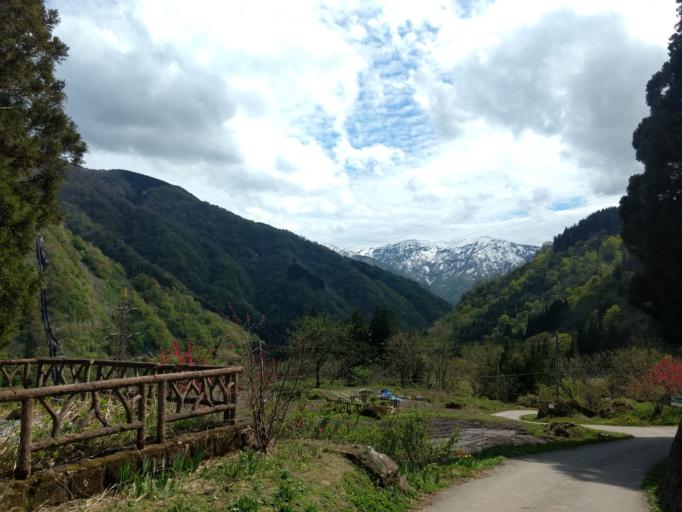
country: JP
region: Toyama
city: Nanto-shi
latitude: 36.4245
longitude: 136.9348
